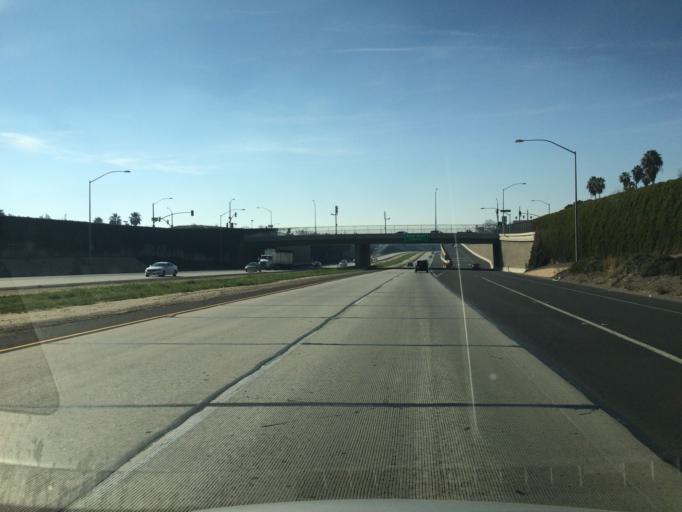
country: US
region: California
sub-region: Tulare County
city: Visalia
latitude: 36.3274
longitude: -119.3240
